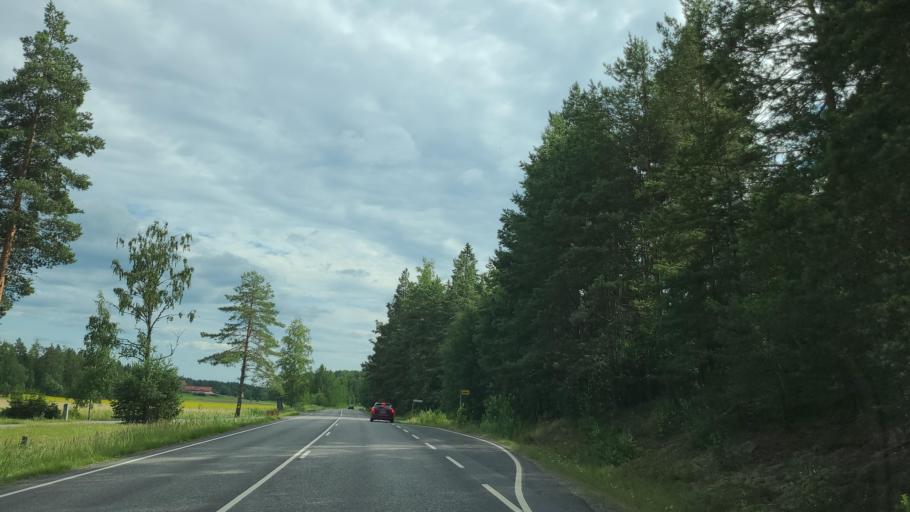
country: FI
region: Varsinais-Suomi
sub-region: Turku
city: Merimasku
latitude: 60.4450
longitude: 21.8971
